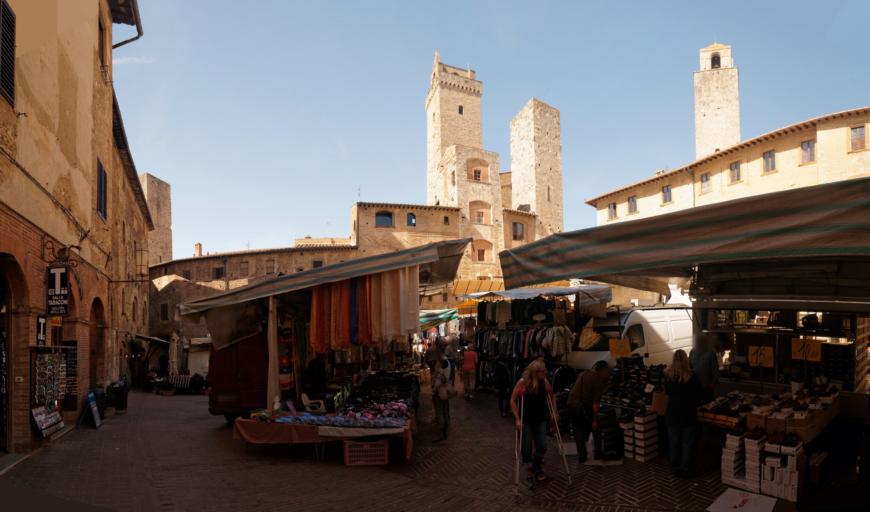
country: IT
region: Tuscany
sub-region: Provincia di Siena
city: San Gimignano
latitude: 43.4674
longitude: 11.0439
